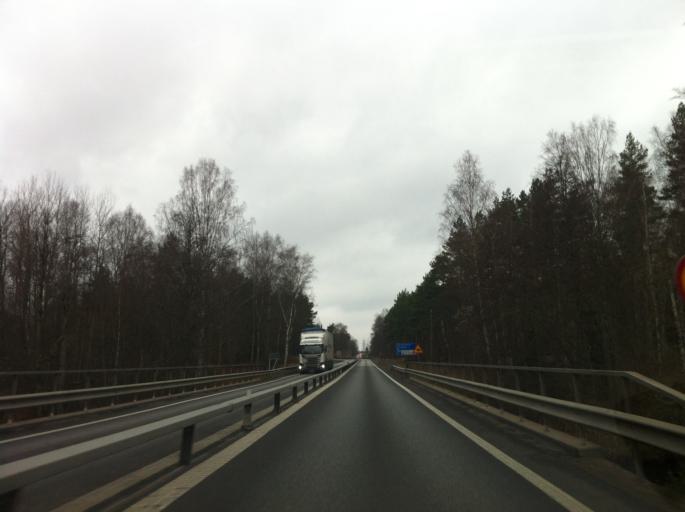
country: SE
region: Joenkoeping
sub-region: Vetlanda Kommun
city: Vetlanda
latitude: 57.4236
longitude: 15.1243
